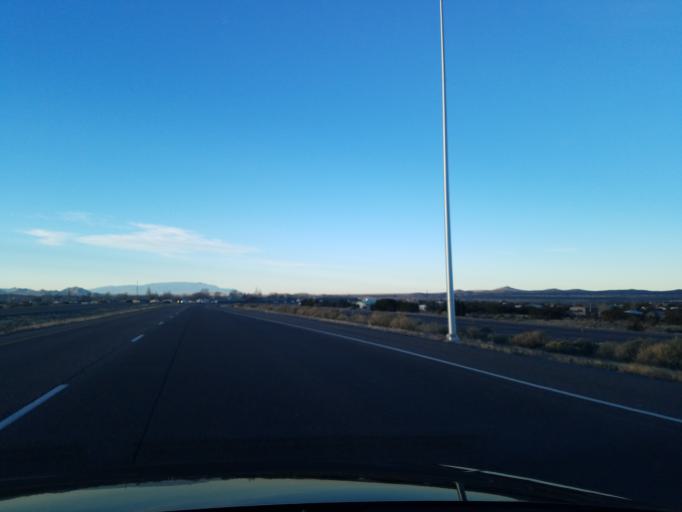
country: US
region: New Mexico
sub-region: Santa Fe County
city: Agua Fria
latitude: 35.6554
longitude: -106.0400
